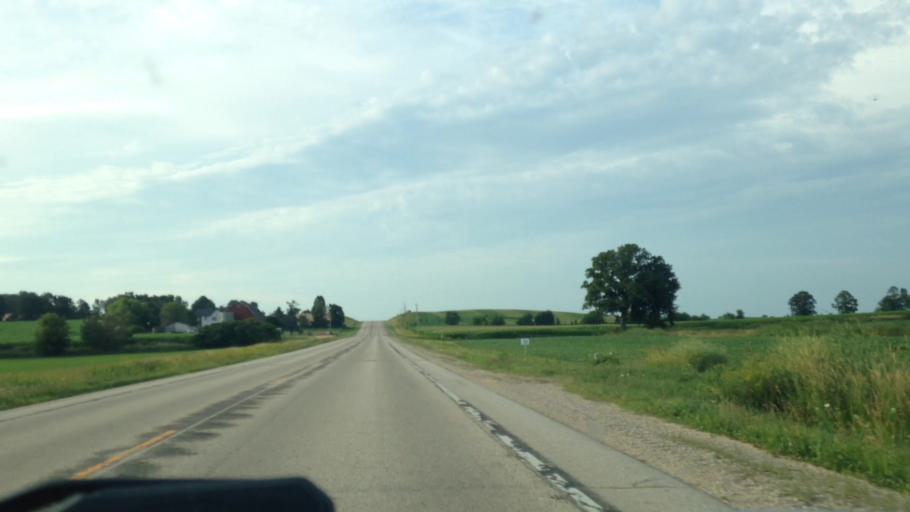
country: US
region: Wisconsin
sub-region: Dodge County
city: Theresa
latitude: 43.4743
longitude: -88.4501
